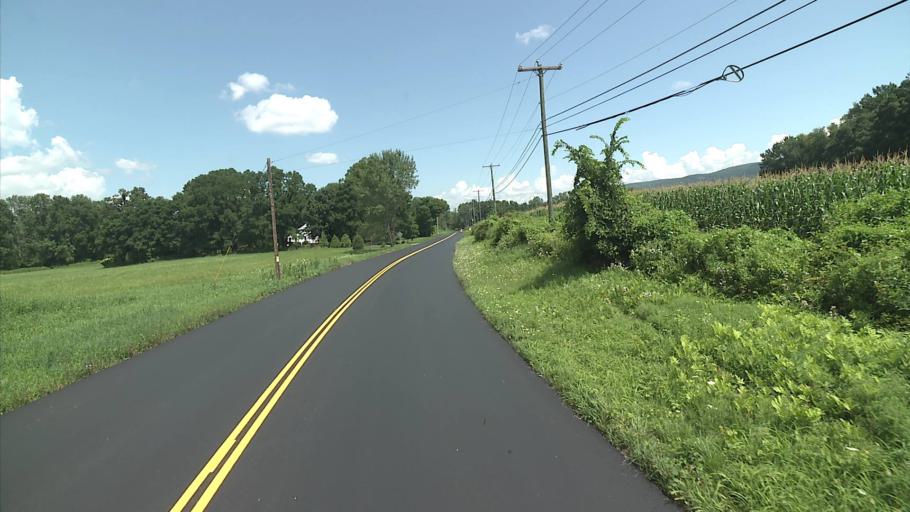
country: US
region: Connecticut
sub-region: Litchfield County
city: Canaan
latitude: 41.9719
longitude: -73.3586
